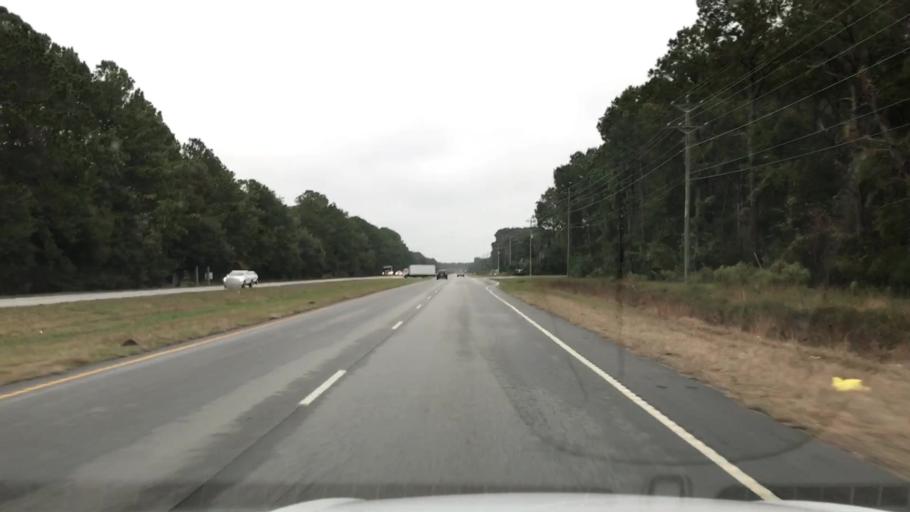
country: US
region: South Carolina
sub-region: Charleston County
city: Isle of Palms
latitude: 32.9081
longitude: -79.7247
